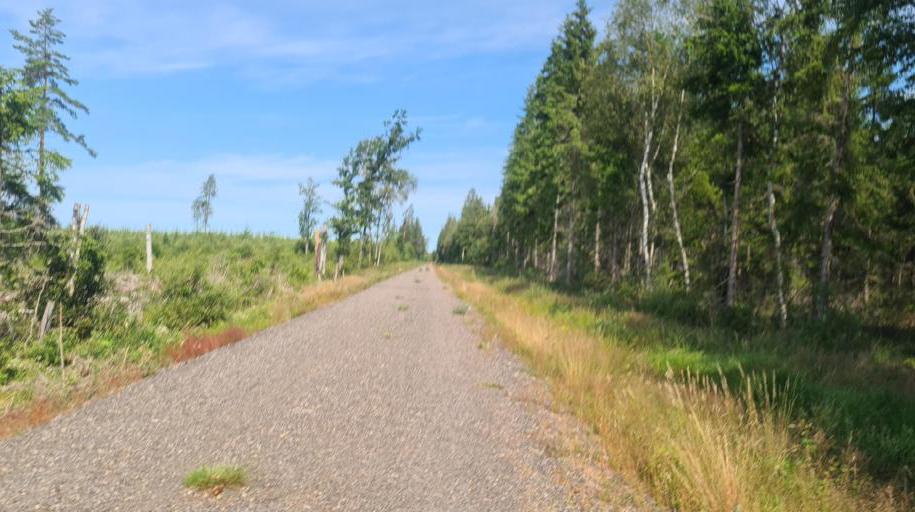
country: SE
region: Kronoberg
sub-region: Ljungby Kommun
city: Lagan
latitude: 56.9802
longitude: 13.9463
